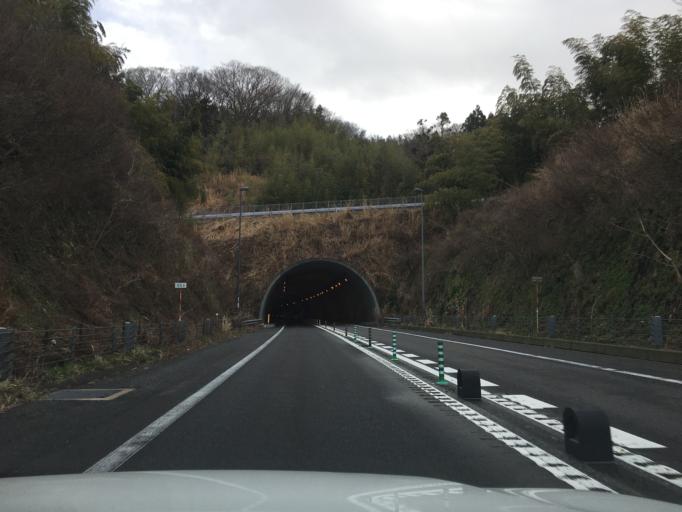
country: JP
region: Yamagata
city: Yuza
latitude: 39.3176
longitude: 140.0165
